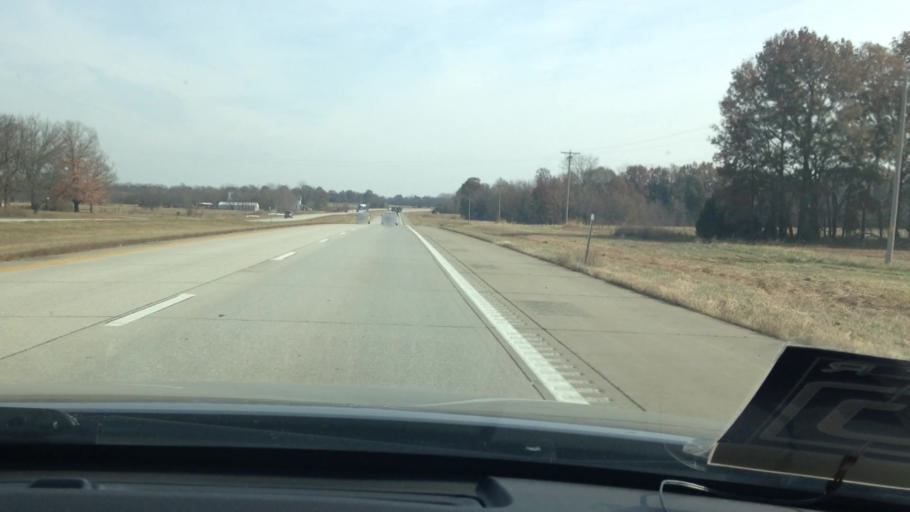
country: US
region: Missouri
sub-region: Henry County
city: Clinton
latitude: 38.4636
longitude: -93.9817
